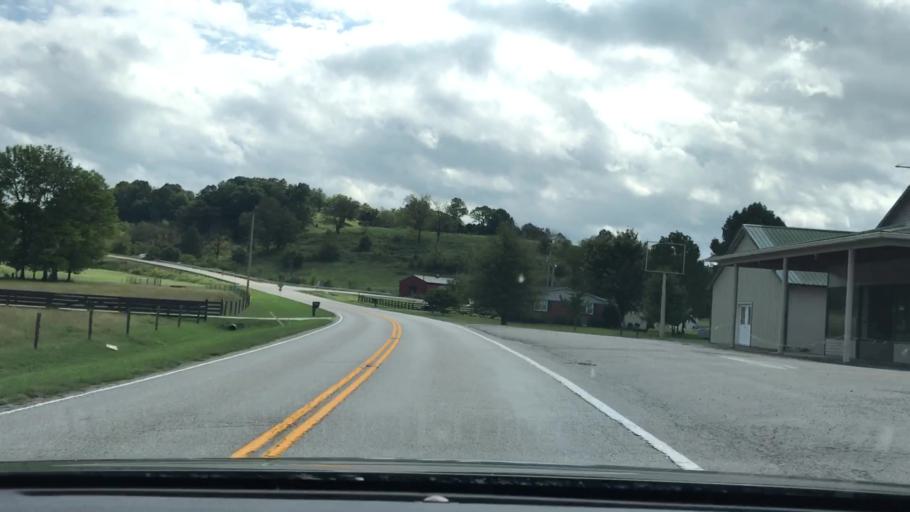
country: US
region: Kentucky
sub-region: Cumberland County
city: Burkesville
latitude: 36.8172
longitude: -85.4584
